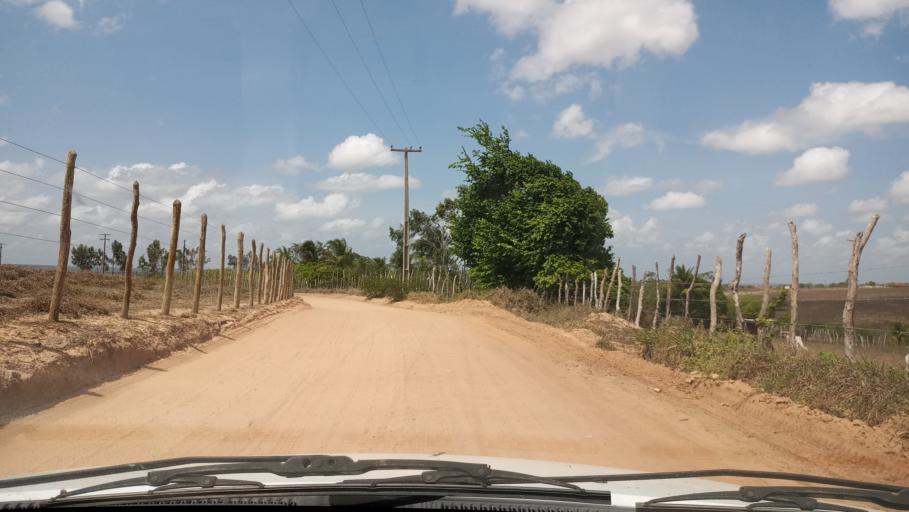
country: BR
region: Rio Grande do Norte
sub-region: Goianinha
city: Goianinha
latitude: -6.3417
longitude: -35.3263
